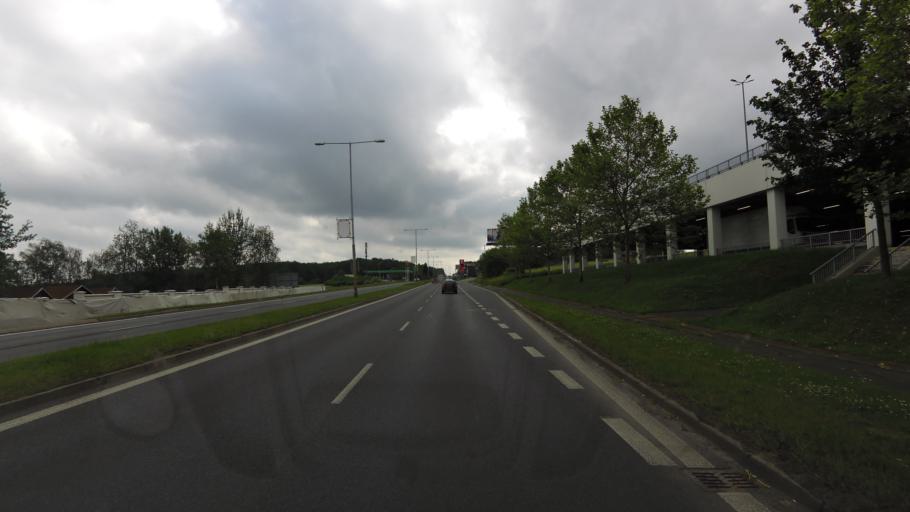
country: CZ
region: Plzensky
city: Stary Plzenec
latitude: 49.7466
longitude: 13.4382
